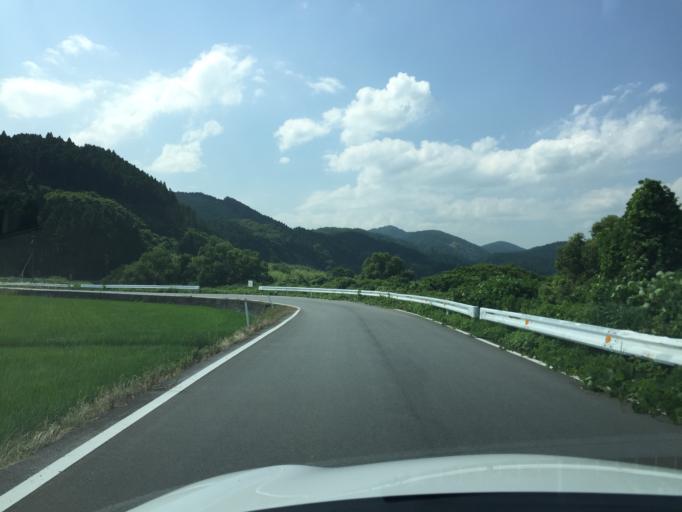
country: JP
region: Ibaraki
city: Kitaibaraki
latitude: 36.9291
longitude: 140.7371
